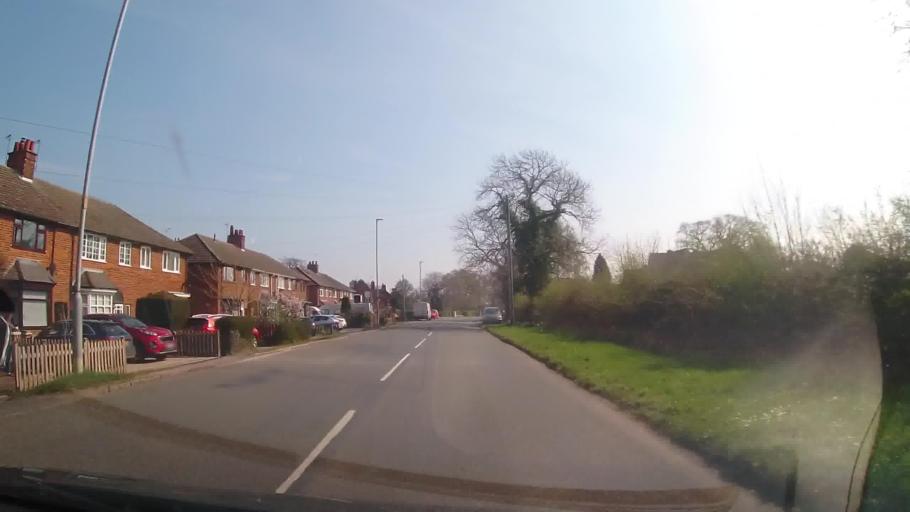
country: GB
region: England
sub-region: Leicestershire
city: Anstey
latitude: 52.6781
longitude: -1.2034
